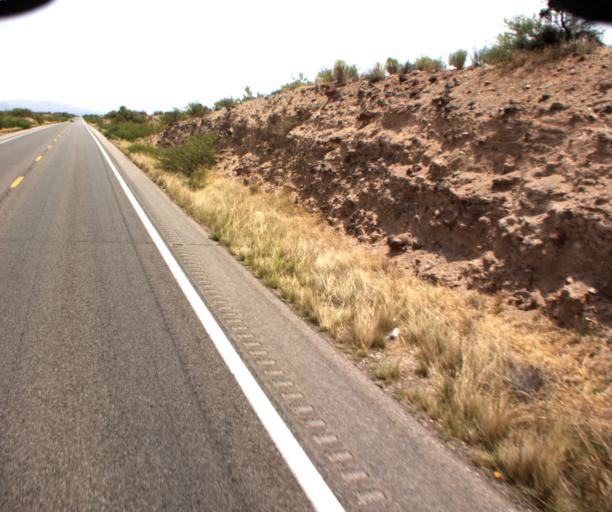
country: US
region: Arizona
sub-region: Gila County
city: Peridot
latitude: 33.3244
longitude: -110.5493
